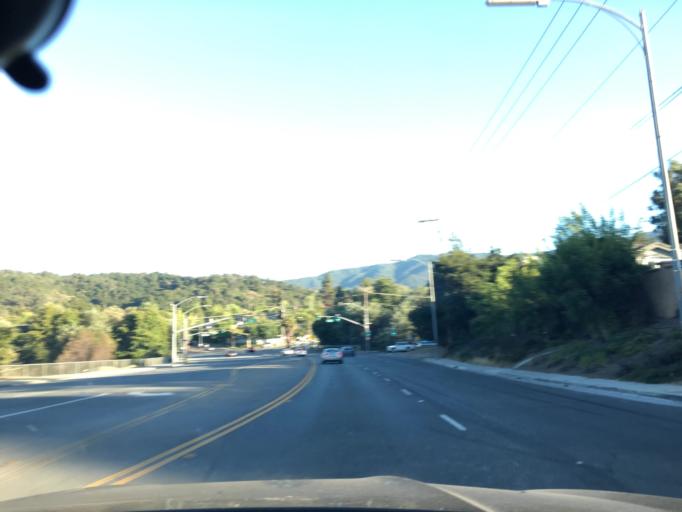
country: US
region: California
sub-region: Santa Clara County
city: Cambrian Park
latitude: 37.2276
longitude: -121.9042
